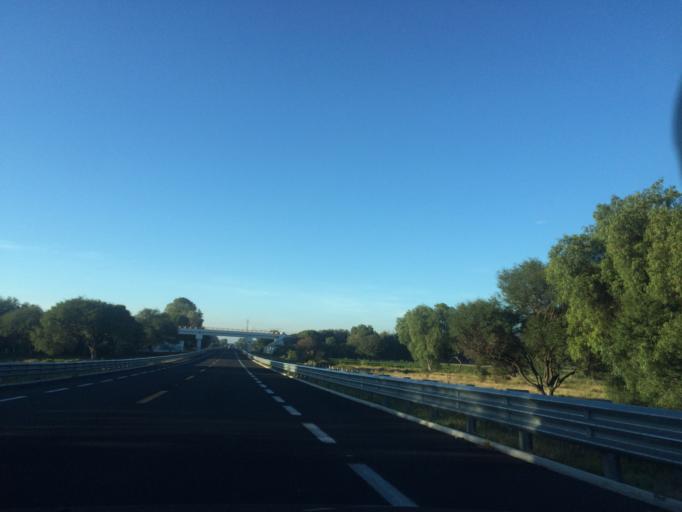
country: MX
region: Puebla
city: Santiago Miahuatlan
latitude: 18.5428
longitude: -97.4608
